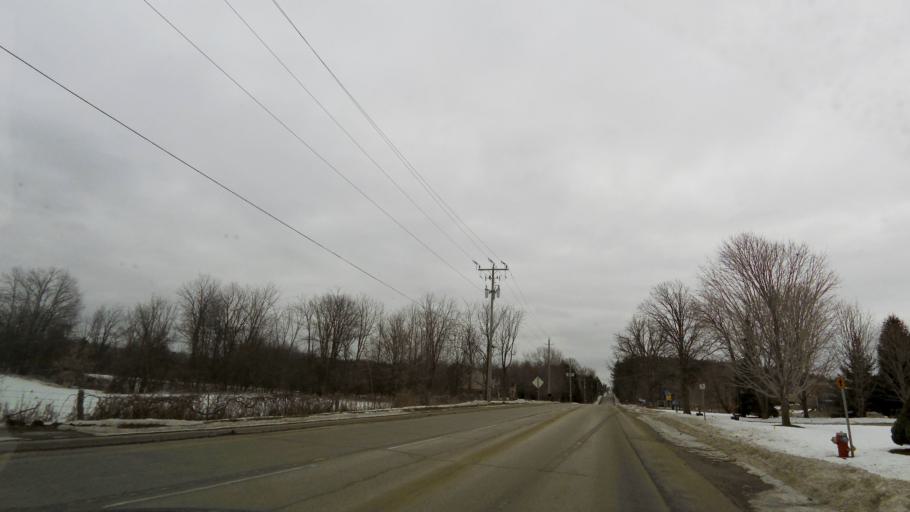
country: CA
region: Ontario
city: Brampton
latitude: 43.8782
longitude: -79.8543
